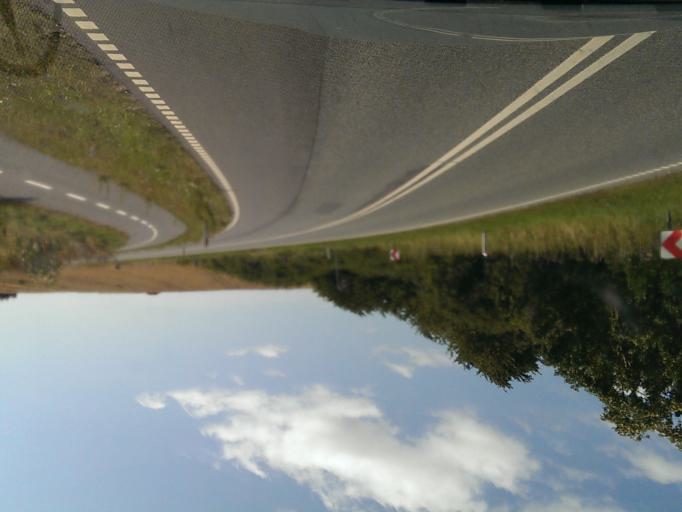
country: DK
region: Central Jutland
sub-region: Syddjurs Kommune
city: Ronde
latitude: 56.2509
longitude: 10.5601
